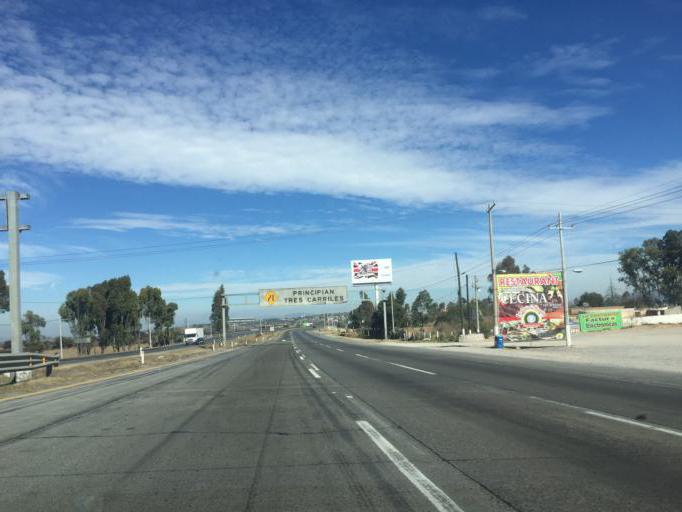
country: MX
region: Queretaro
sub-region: San Juan del Rio
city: Paso de Mata
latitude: 20.3006
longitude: -99.9342
